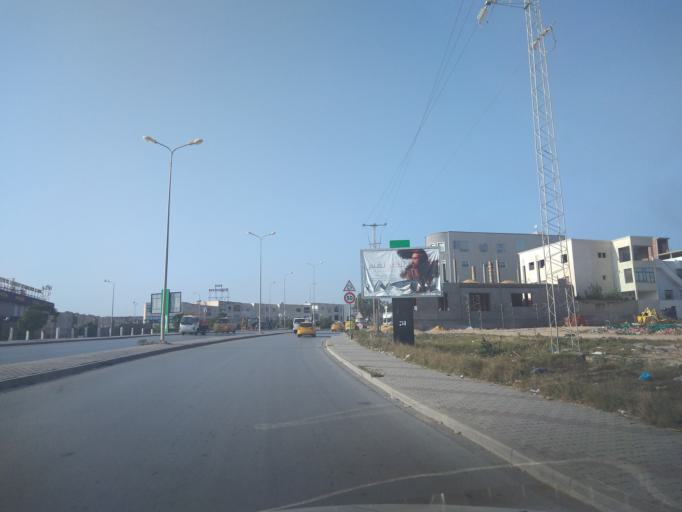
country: TN
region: Manouba
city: Manouba
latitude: 36.7863
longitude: 10.0823
